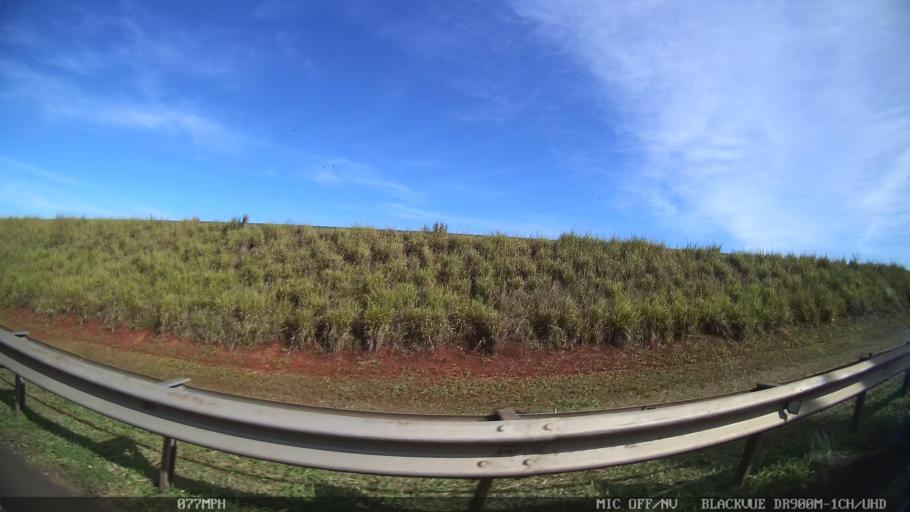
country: BR
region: Sao Paulo
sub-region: Cordeiropolis
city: Cordeiropolis
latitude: -22.4803
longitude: -47.3991
